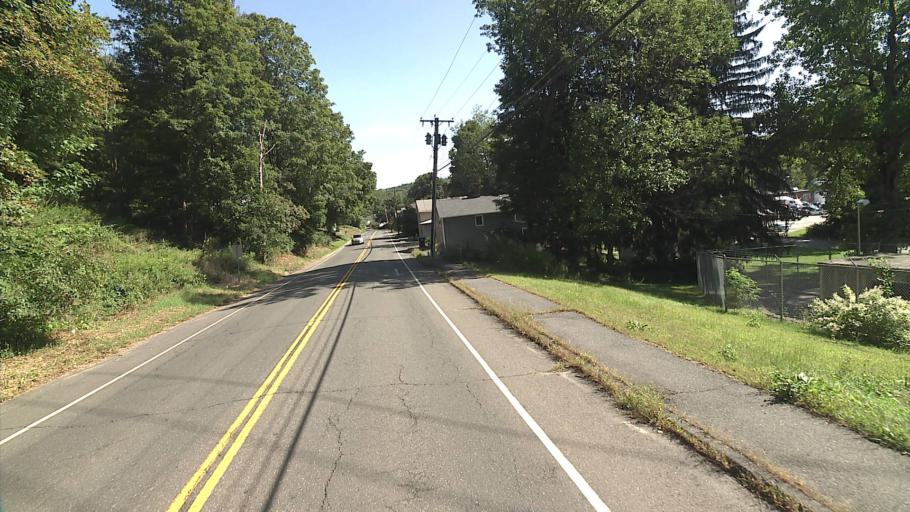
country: US
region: Connecticut
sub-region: Litchfield County
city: Thomaston
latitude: 41.6770
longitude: -73.0700
